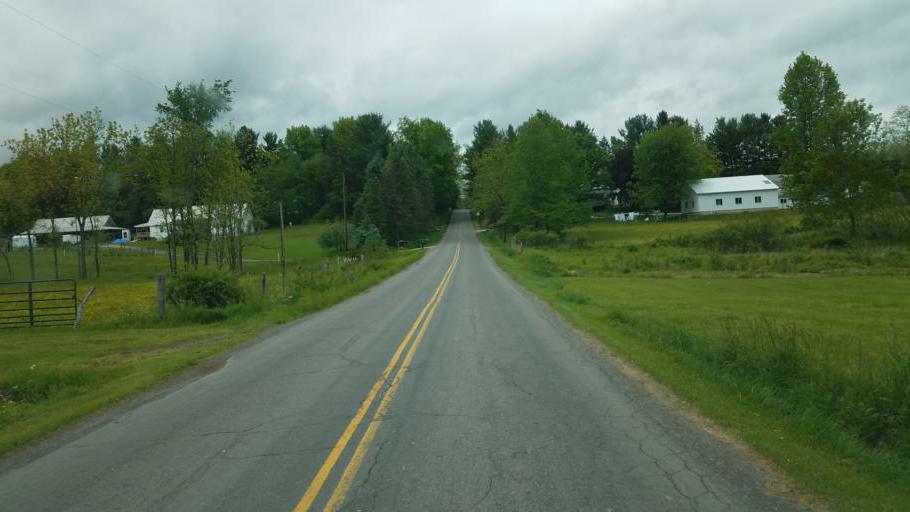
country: US
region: Ohio
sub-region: Geauga County
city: Middlefield
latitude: 41.4171
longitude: -80.9738
